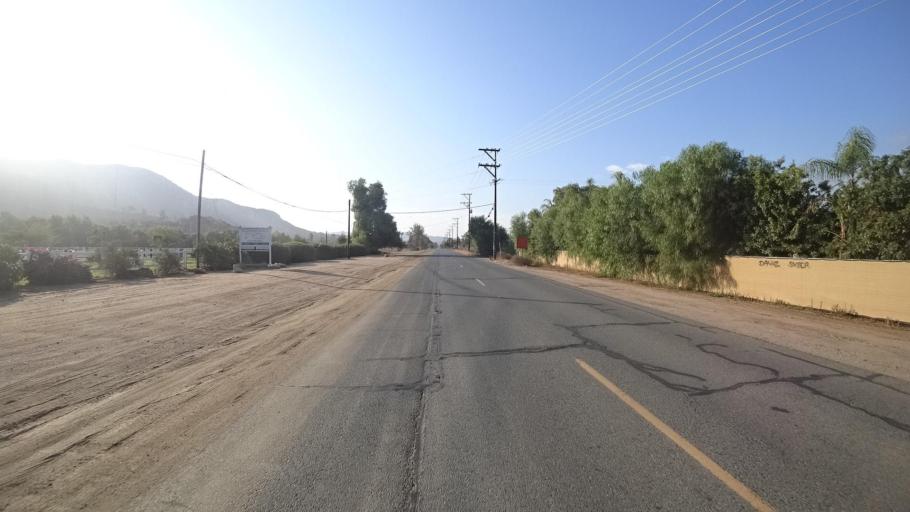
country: US
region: California
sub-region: San Diego County
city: Eucalyptus Hills
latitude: 32.8972
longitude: -116.9294
